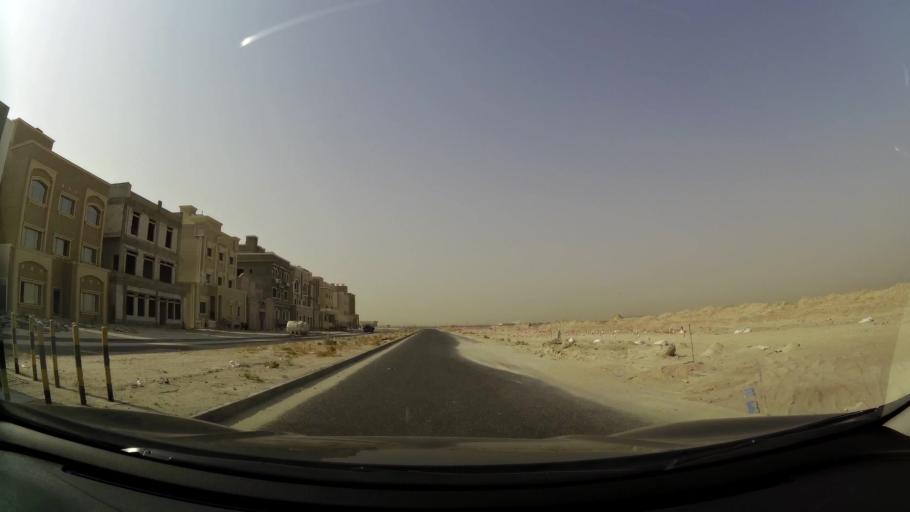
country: KW
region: Muhafazat al Jahra'
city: Al Jahra'
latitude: 29.3527
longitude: 47.7407
